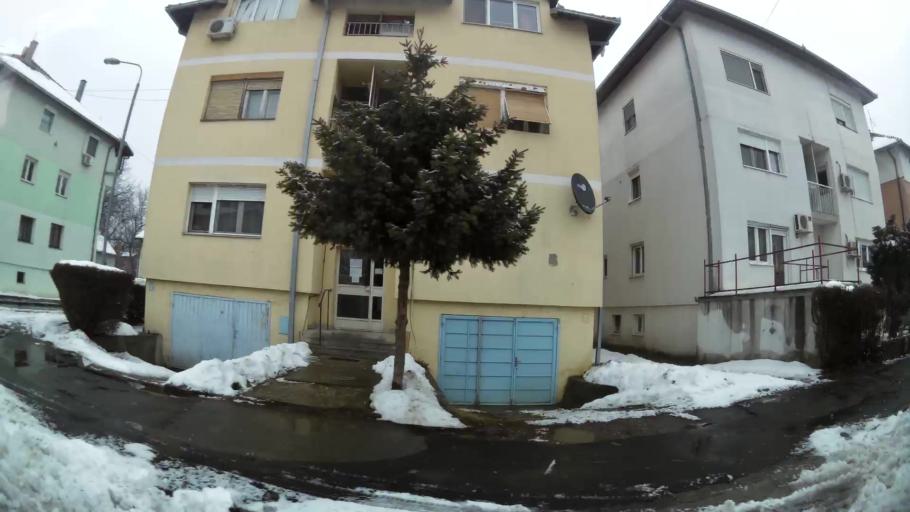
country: RS
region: Central Serbia
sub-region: Belgrade
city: Zemun
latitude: 44.8739
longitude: 20.3180
